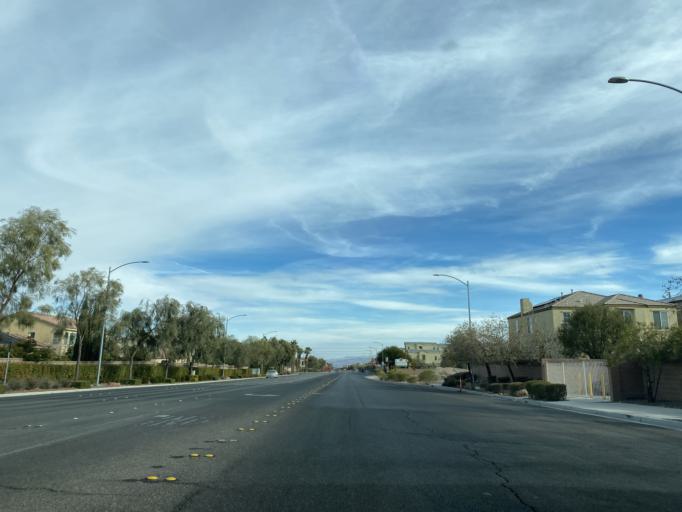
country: US
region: Nevada
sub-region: Clark County
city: Enterprise
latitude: 36.0411
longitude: -115.2520
